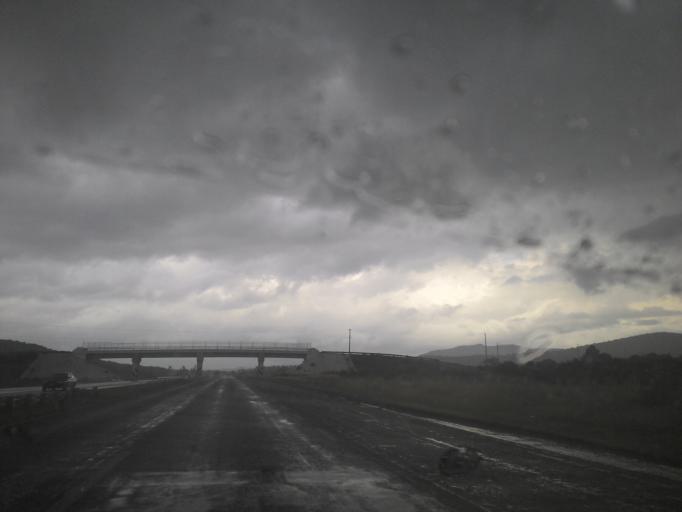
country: MX
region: Hidalgo
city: Zempoala
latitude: 19.9003
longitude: -98.6057
